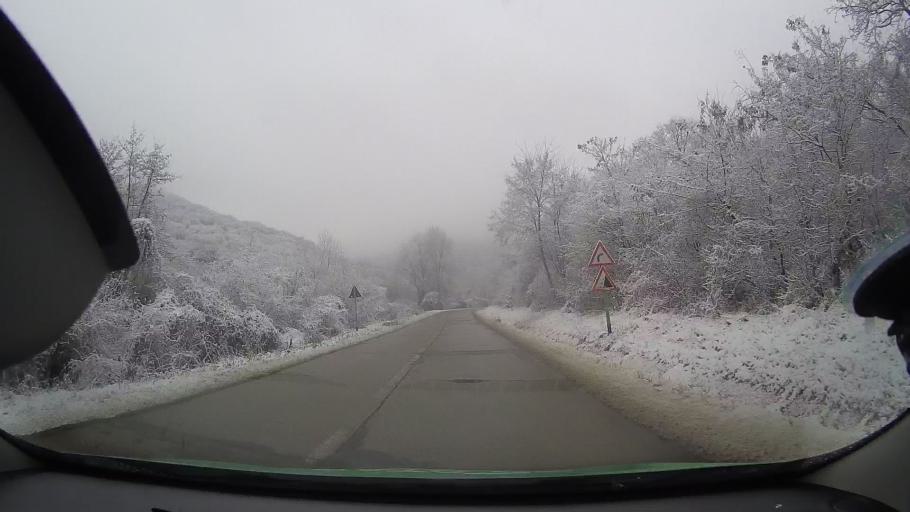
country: RO
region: Cluj
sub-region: Comuna Moldovenesti
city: Moldovenesti
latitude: 46.5060
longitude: 23.6523
